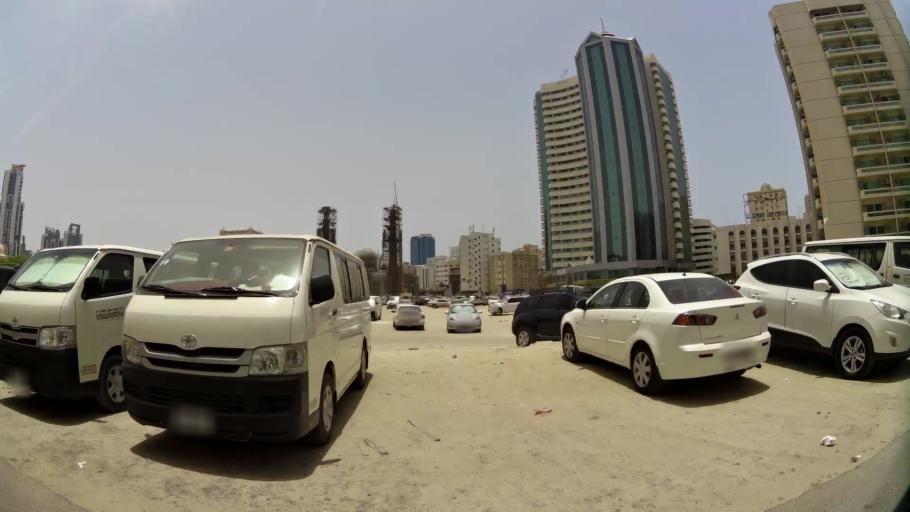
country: AE
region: Ash Shariqah
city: Sharjah
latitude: 25.3540
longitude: 55.3924
